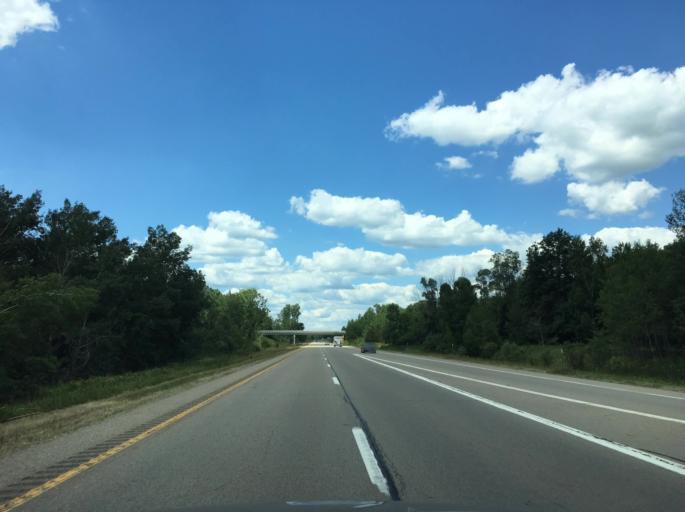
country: US
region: Michigan
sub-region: Clare County
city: Clare
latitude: 43.8806
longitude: -84.7839
